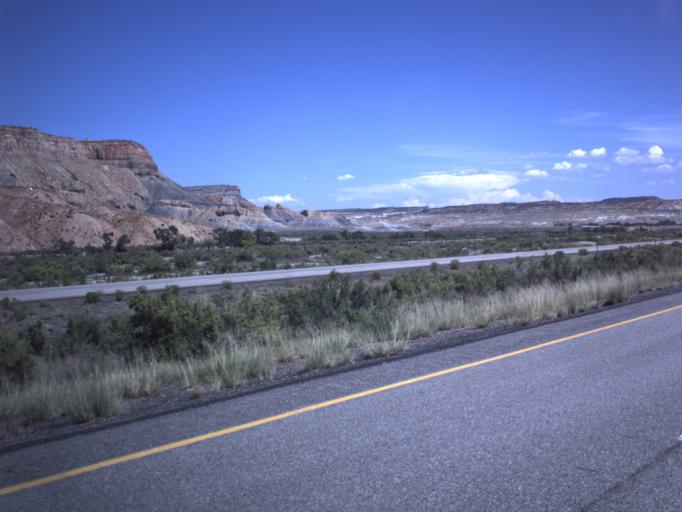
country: US
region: Utah
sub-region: Emery County
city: Ferron
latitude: 38.8095
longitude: -111.2335
